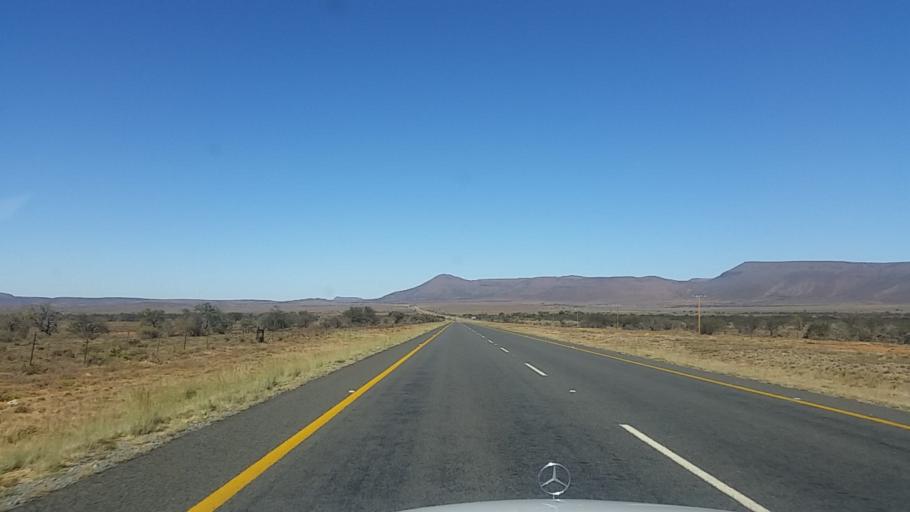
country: ZA
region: Eastern Cape
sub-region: Cacadu District Municipality
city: Graaff-Reinet
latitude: -31.9979
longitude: 24.6718
